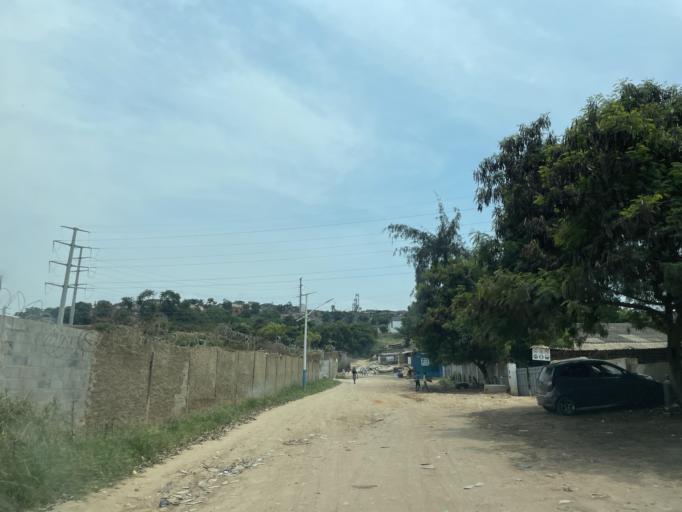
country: AO
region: Luanda
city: Luanda
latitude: -8.8059
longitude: 13.2572
